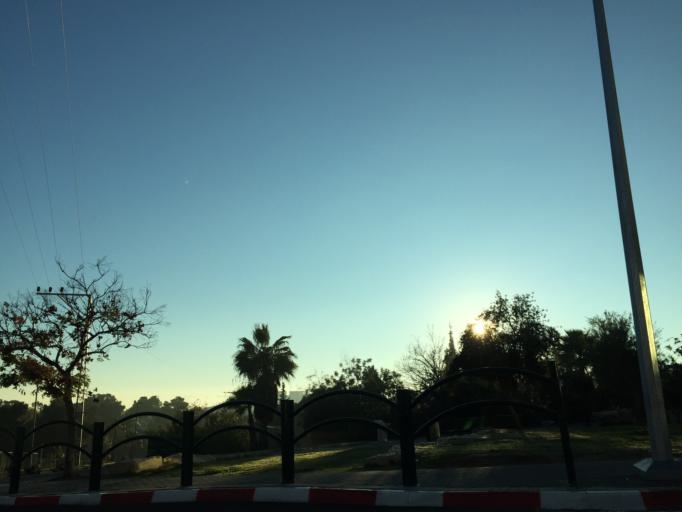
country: IL
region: Southern District
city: Mitzpe Ramon
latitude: 30.6116
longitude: 34.8008
